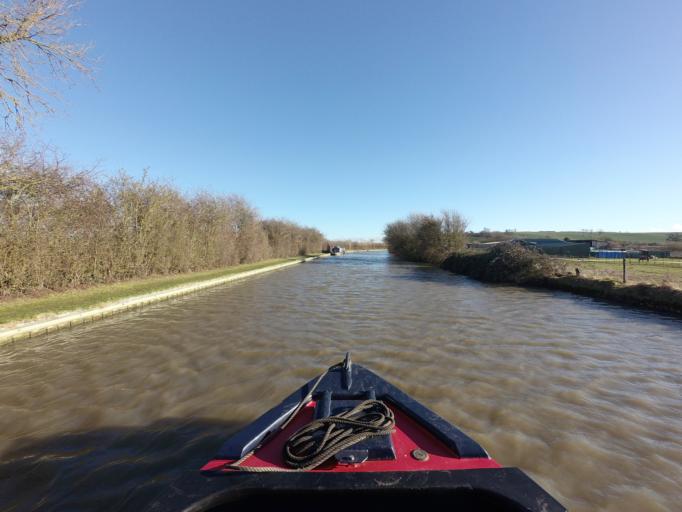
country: GB
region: England
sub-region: Northamptonshire
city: Bugbrooke
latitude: 52.1974
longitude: -0.9846
